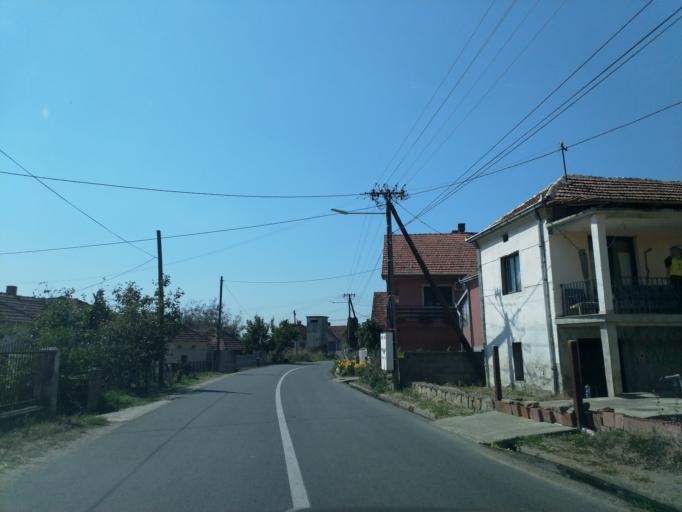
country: RS
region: Central Serbia
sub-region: Rasinski Okrug
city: Krusevac
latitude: 43.6235
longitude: 21.3507
